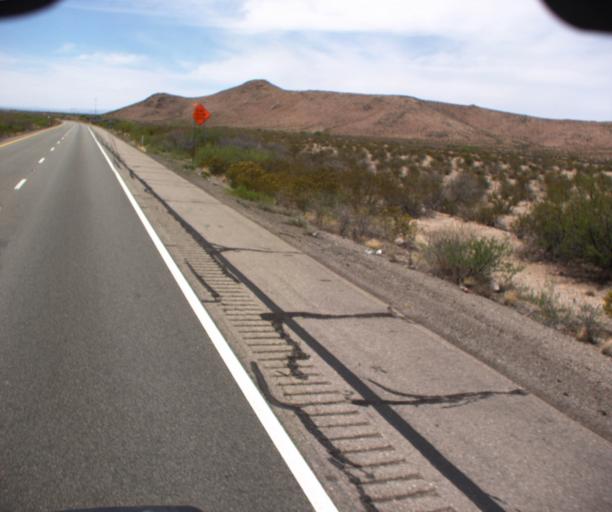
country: US
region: New Mexico
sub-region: Hidalgo County
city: Lordsburg
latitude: 32.2363
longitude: -109.0782
